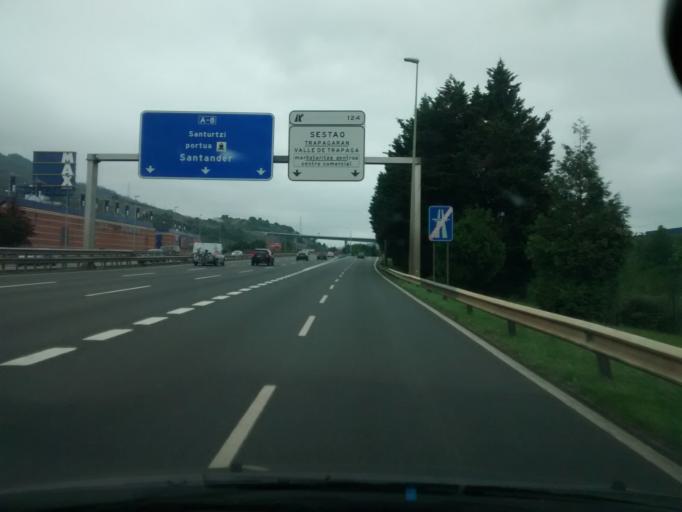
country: ES
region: Basque Country
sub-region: Bizkaia
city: Barakaldo
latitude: 43.2892
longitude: -3.0057
